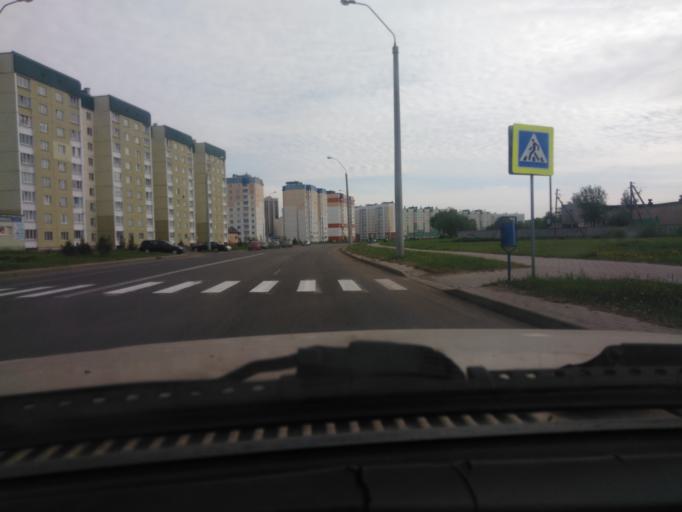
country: BY
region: Mogilev
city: Mahilyow
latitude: 53.9122
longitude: 30.2847
